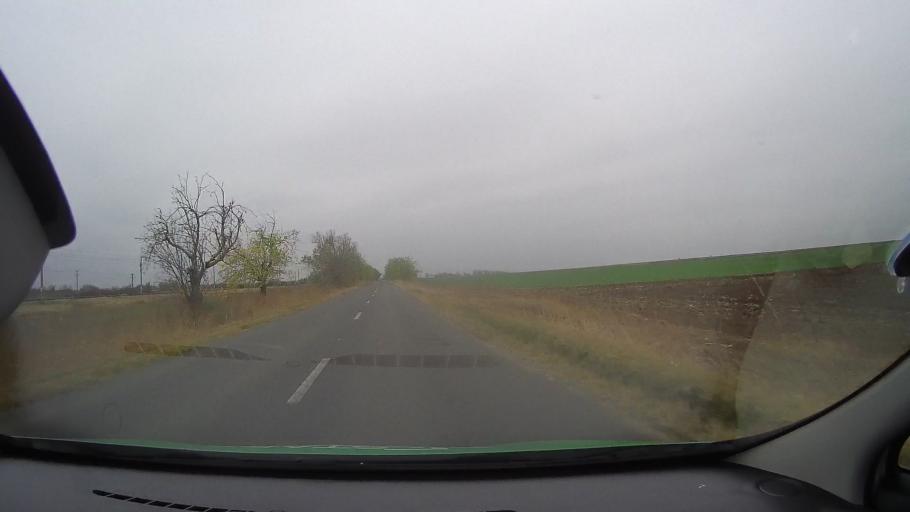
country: RO
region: Ialomita
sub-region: Comuna Valea Ciorii
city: Valea Ciorii
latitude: 44.6939
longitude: 27.6038
